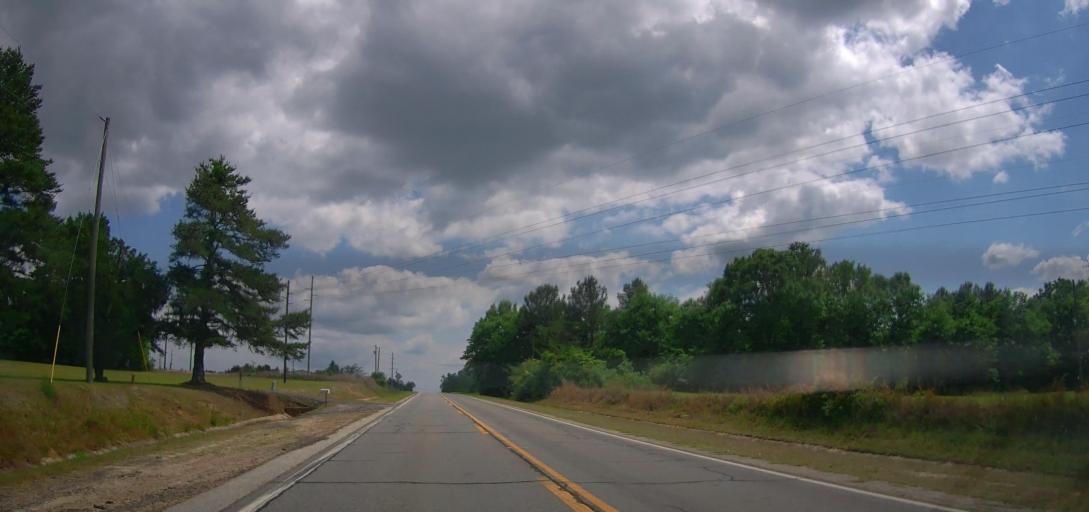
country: US
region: Georgia
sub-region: Laurens County
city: East Dublin
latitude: 32.5128
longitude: -82.8408
